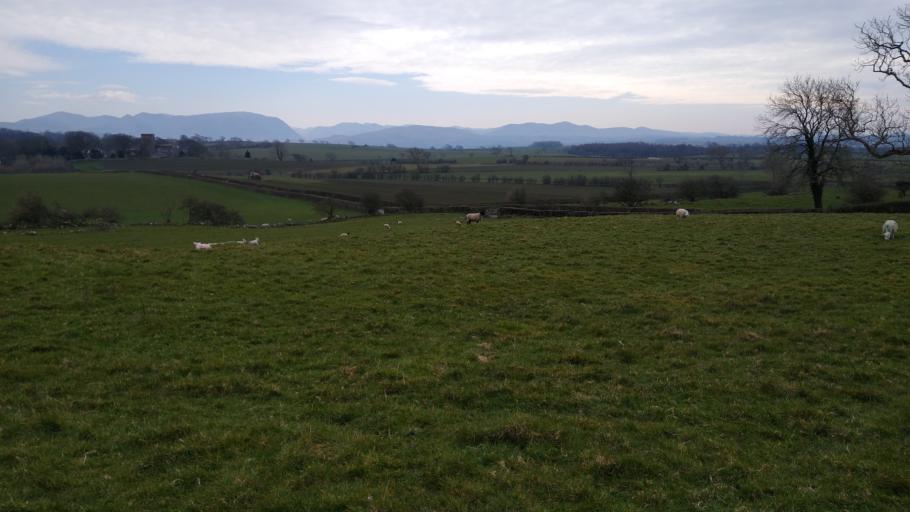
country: GB
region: England
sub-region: Cumbria
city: Cockermouth
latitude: 54.6948
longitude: -3.3771
